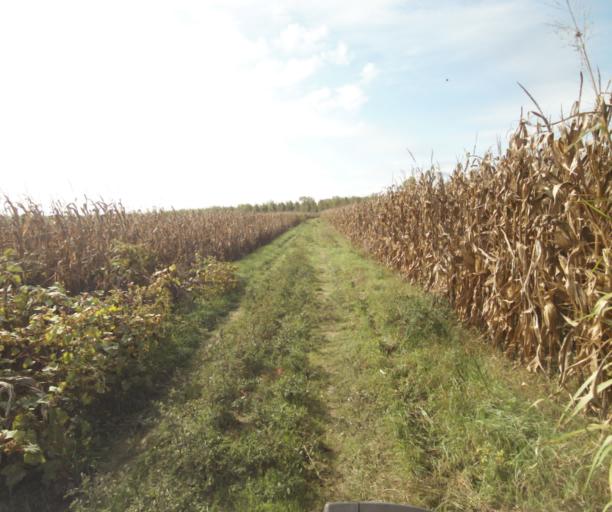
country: FR
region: Midi-Pyrenees
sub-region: Departement du Tarn-et-Garonne
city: Finhan
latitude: 43.9077
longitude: 1.2118
